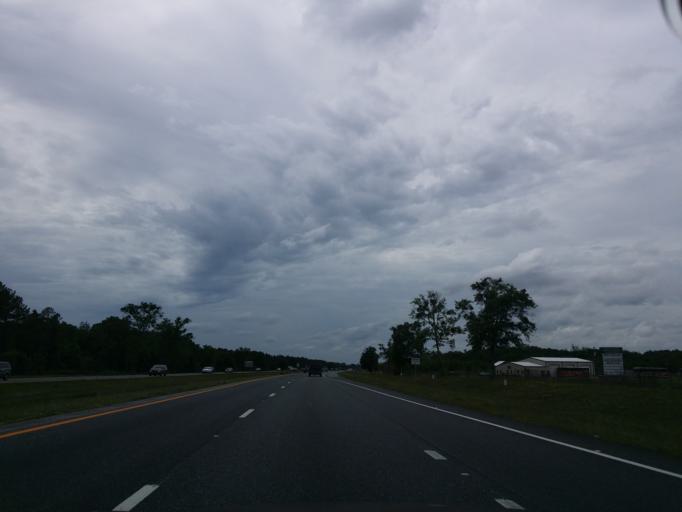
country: US
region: Florida
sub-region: Madison County
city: Madison
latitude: 30.3813
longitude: -83.3040
